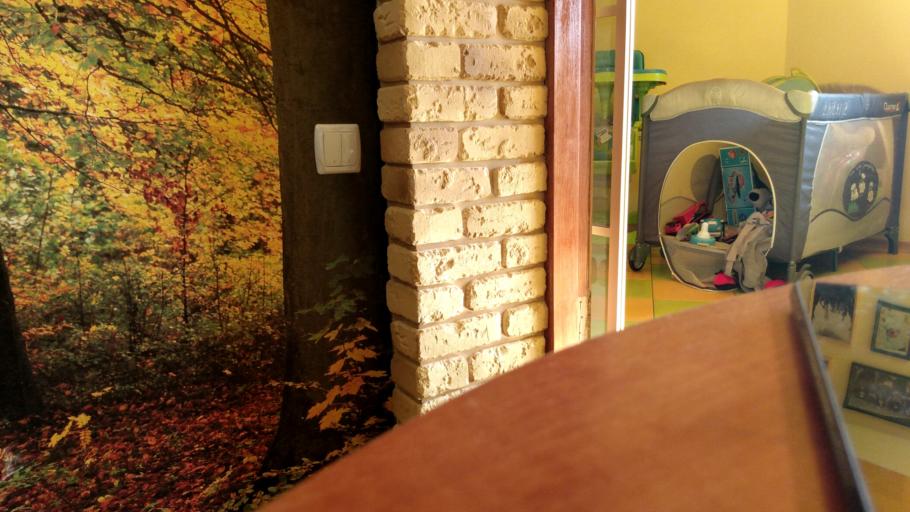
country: RU
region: Tverskaya
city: Radchenko
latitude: 56.6854
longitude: 36.4467
